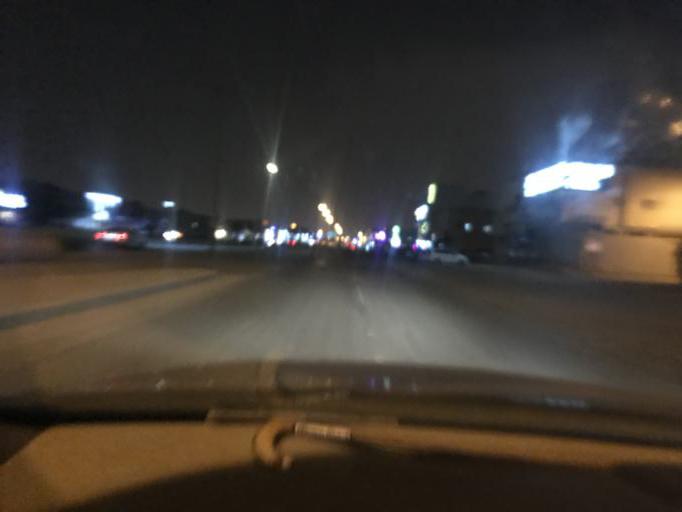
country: SA
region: Ar Riyad
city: Riyadh
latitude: 24.7999
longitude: 46.6966
